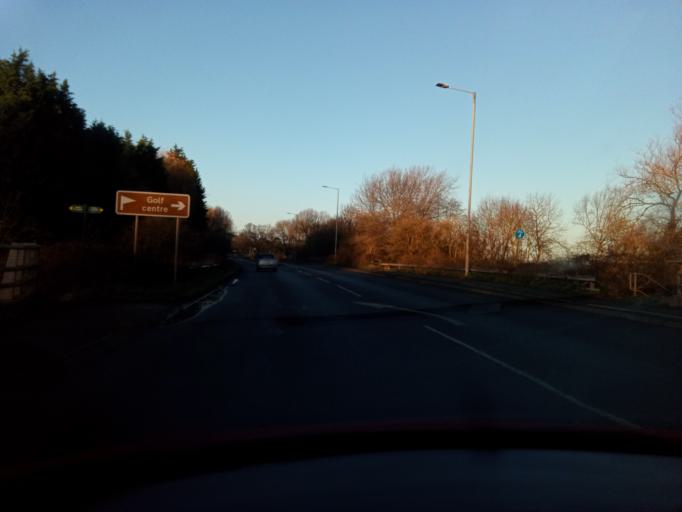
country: GB
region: England
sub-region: Leicestershire
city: Hathern
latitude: 52.7845
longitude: -1.2338
